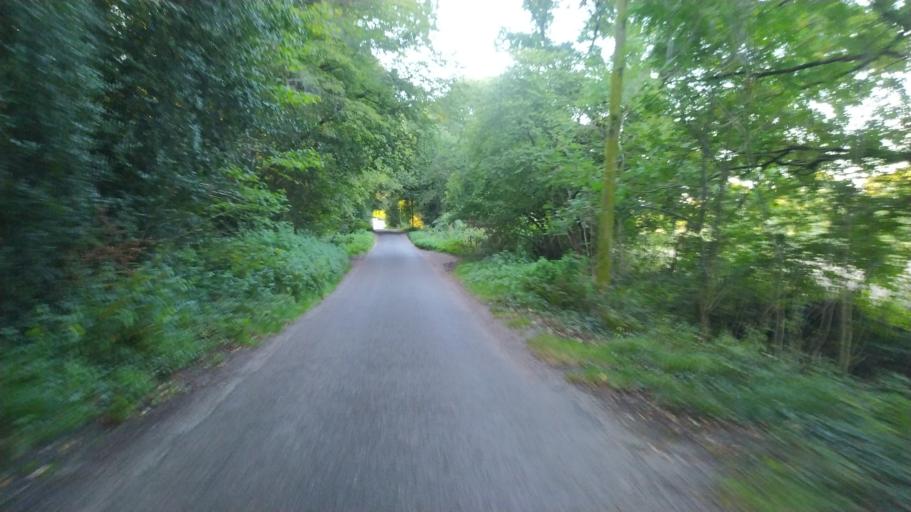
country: GB
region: England
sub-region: Hampshire
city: Lyndhurst
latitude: 50.8663
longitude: -1.5820
